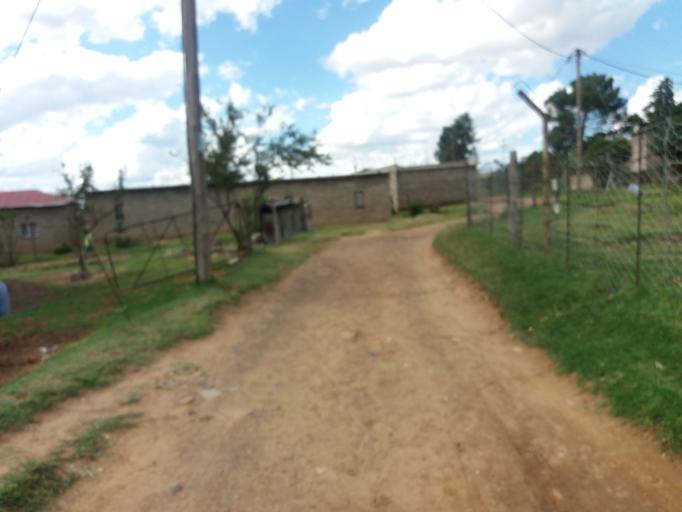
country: LS
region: Maseru
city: Maseru
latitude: -29.3670
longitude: 27.5055
